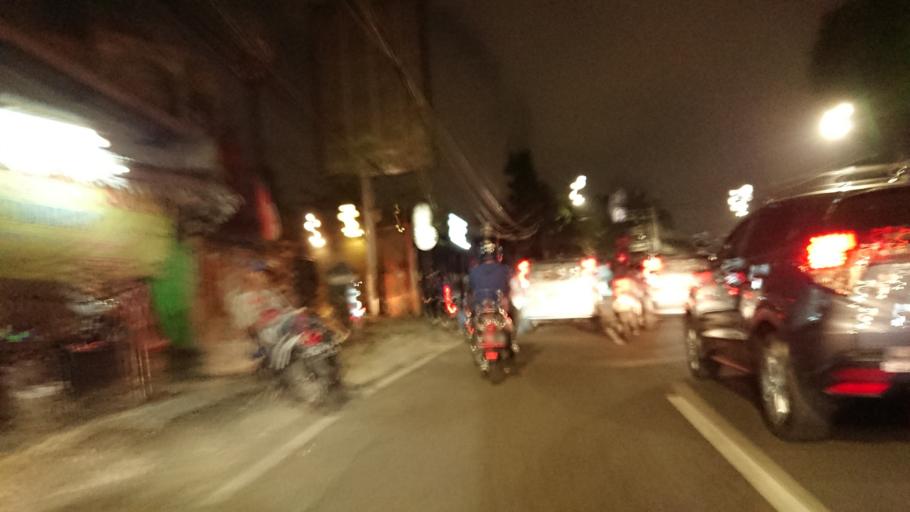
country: ID
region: Jakarta Raya
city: Jakarta
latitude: -6.1978
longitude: 106.8036
